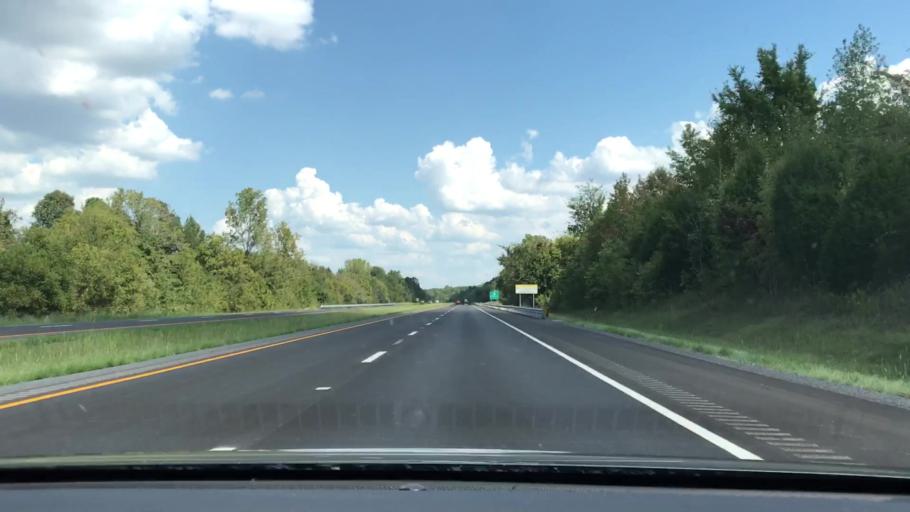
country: US
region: Kentucky
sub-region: Lyon County
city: Eddyville
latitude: 37.0906
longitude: -88.0542
